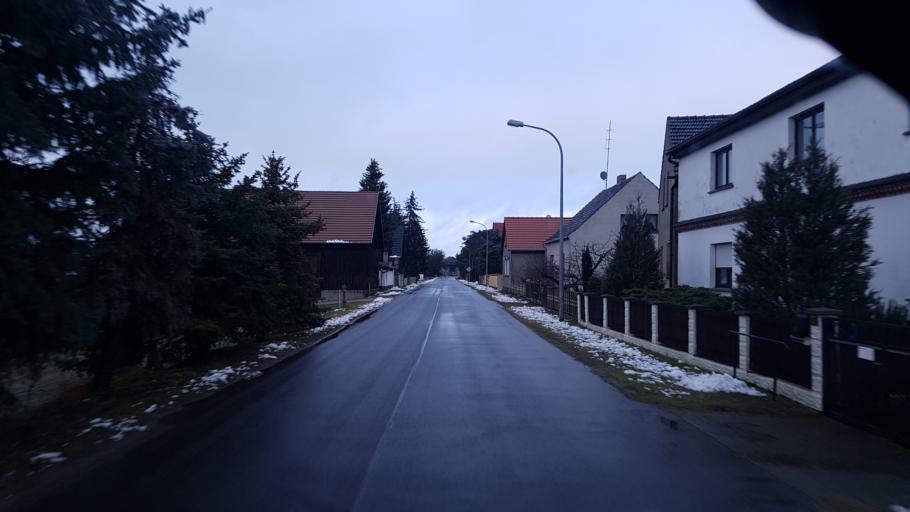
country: DE
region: Brandenburg
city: Janschwalde
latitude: 51.8655
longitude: 14.5092
